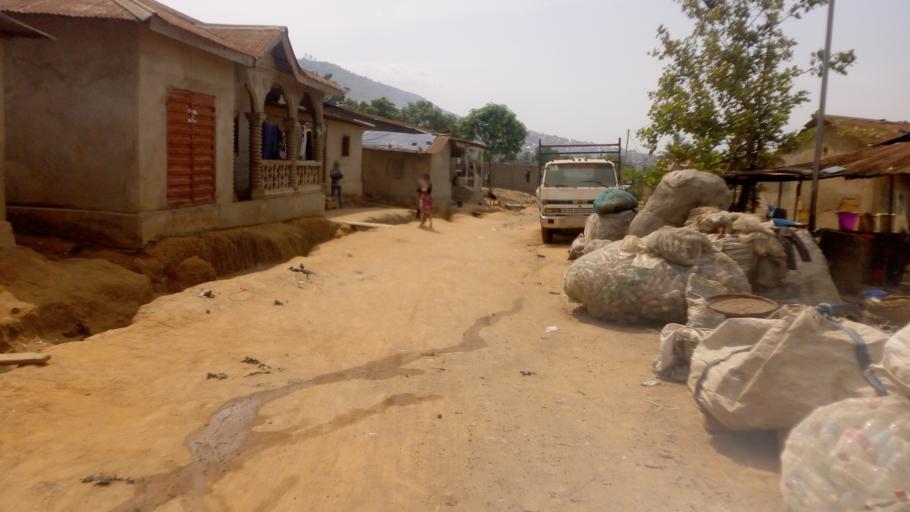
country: SL
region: Western Area
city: Waterloo
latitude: 8.3273
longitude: -13.0650
